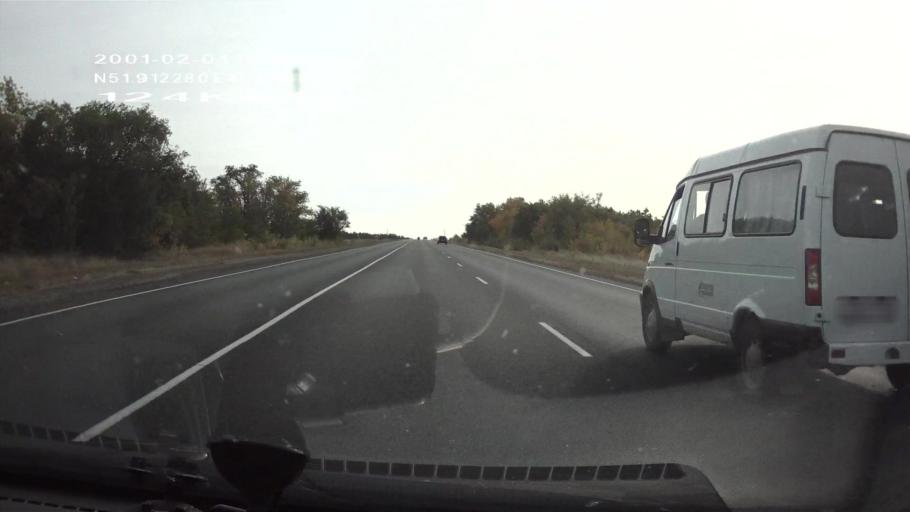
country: RU
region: Saratov
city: Sinodskoye
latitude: 51.9113
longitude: 46.5535
